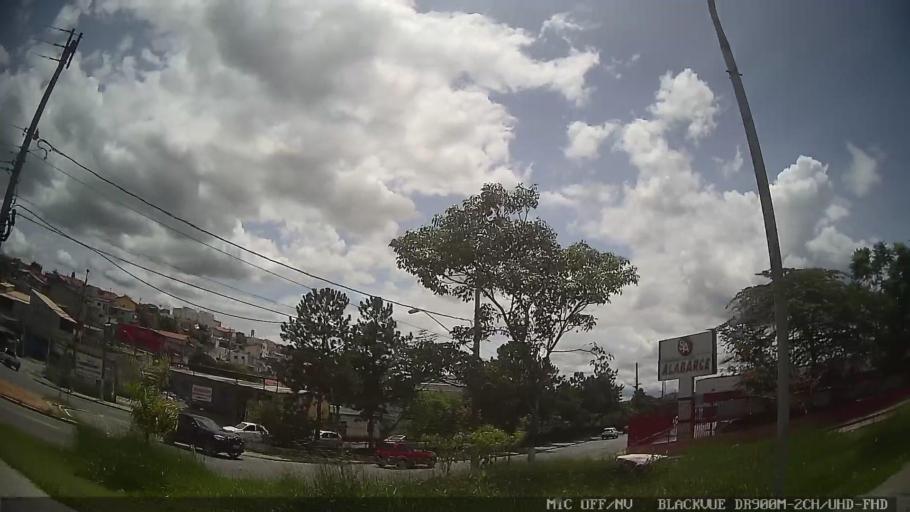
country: BR
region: Sao Paulo
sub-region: Mogi das Cruzes
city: Mogi das Cruzes
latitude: -23.5477
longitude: -46.2037
